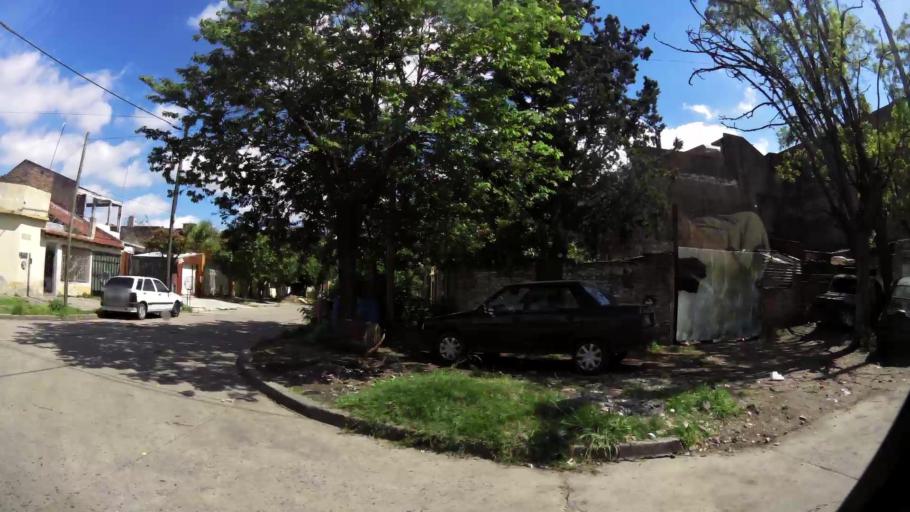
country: AR
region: Buenos Aires
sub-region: Partido de Lanus
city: Lanus
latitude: -34.6705
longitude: -58.4257
